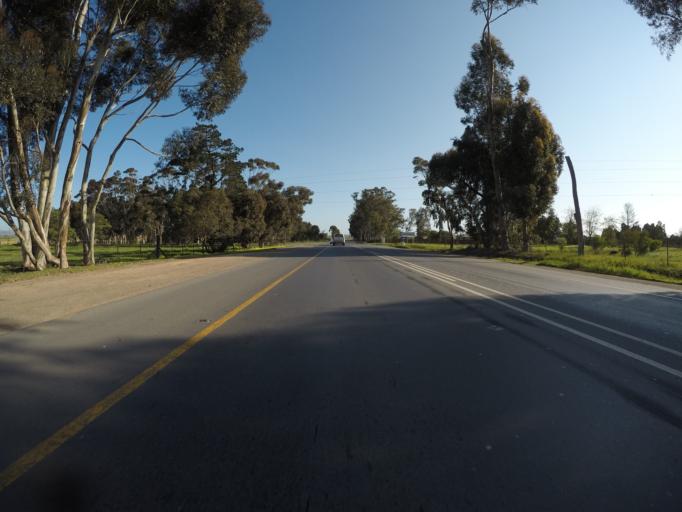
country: ZA
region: Western Cape
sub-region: City of Cape Town
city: Kraaifontein
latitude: -33.7932
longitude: 18.6954
